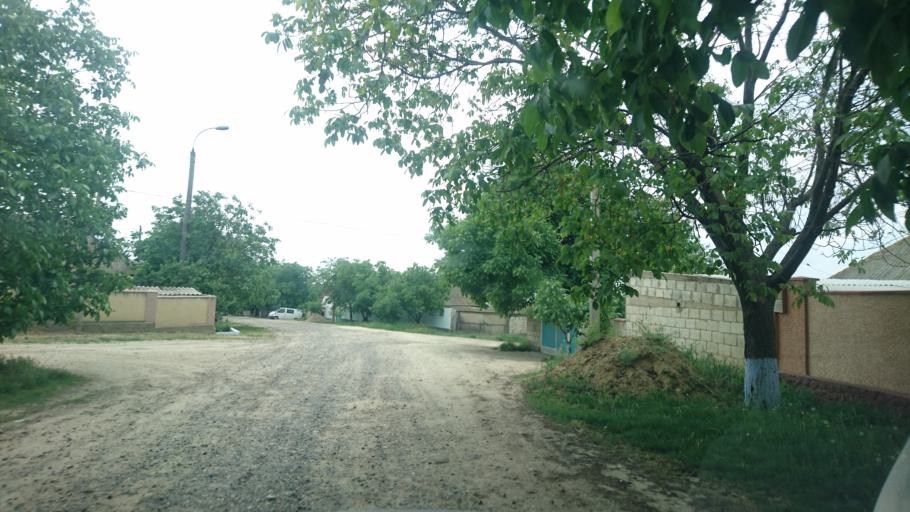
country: MD
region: Telenesti
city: Cocieri
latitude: 47.3554
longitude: 29.1125
